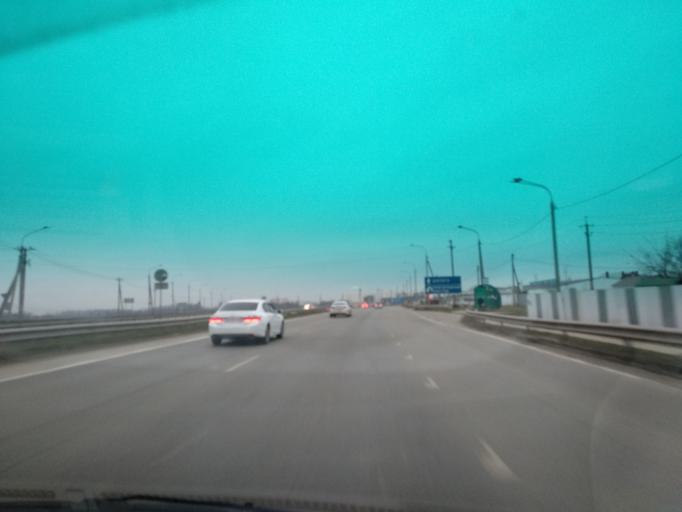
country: RU
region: Krasnodarskiy
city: Pashkovskiy
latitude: 45.0564
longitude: 39.1315
